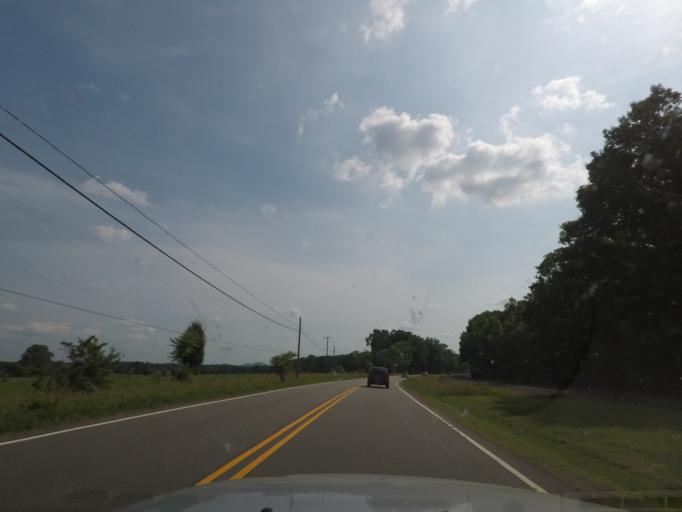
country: US
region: Virginia
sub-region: Buckingham County
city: Buckingham
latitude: 37.5463
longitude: -78.4456
